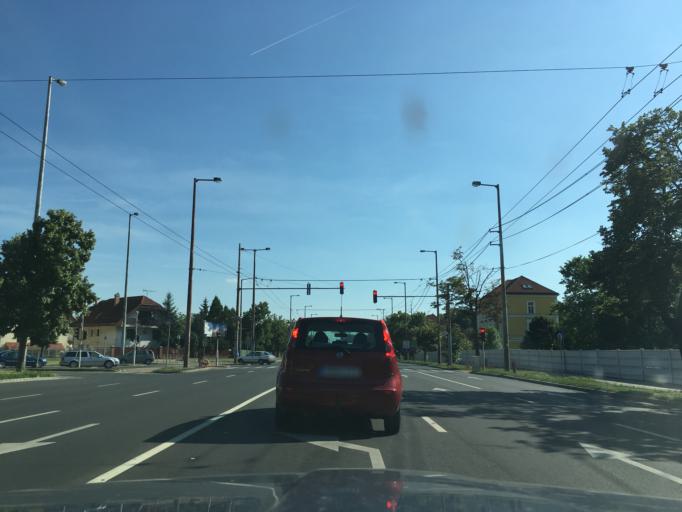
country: HU
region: Hajdu-Bihar
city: Debrecen
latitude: 47.5443
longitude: 21.6429
